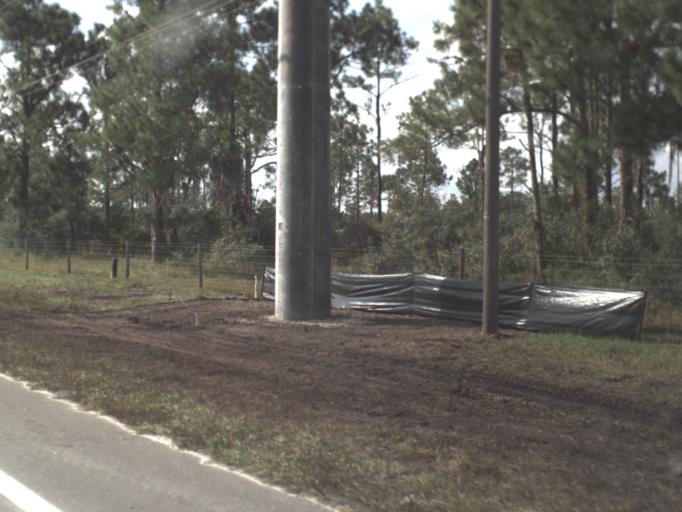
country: US
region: Florida
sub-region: Sarasota County
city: The Meadows
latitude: 27.4753
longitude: -82.3478
